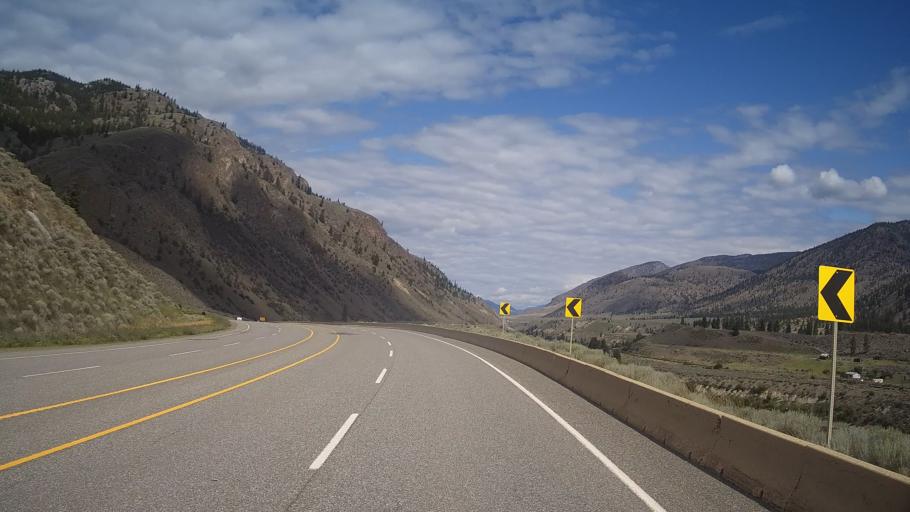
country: CA
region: British Columbia
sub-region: Thompson-Nicola Regional District
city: Ashcroft
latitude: 50.5163
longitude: -121.2819
